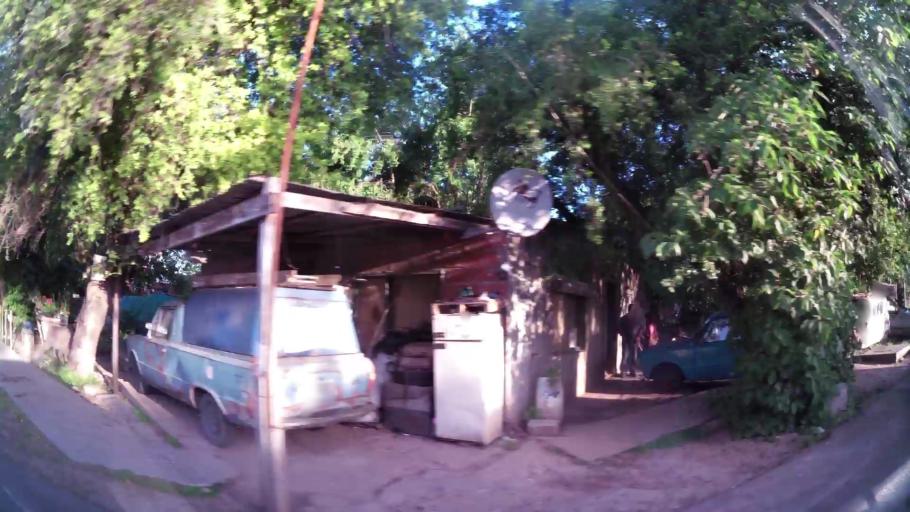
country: AR
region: Buenos Aires
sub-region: Partido de Tigre
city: Tigre
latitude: -34.4496
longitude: -58.6553
